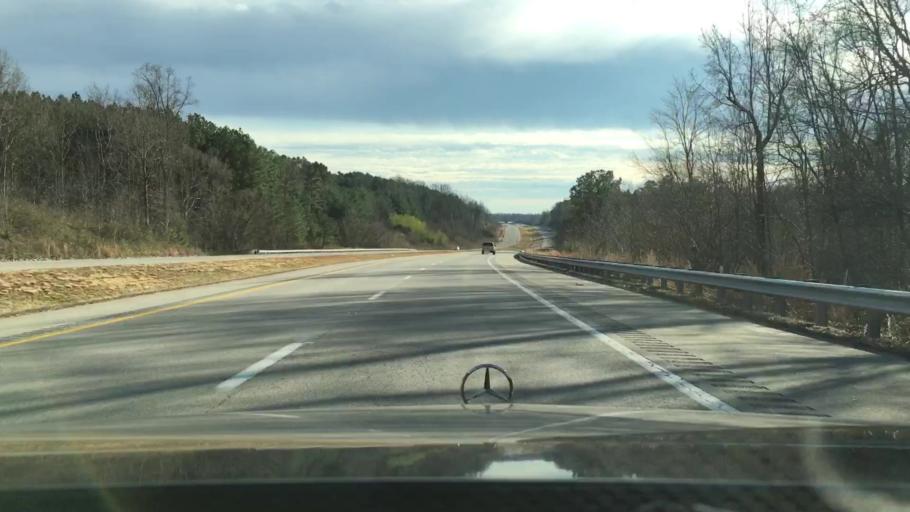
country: US
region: Virginia
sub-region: City of Danville
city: Danville
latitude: 36.6359
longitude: -79.3647
